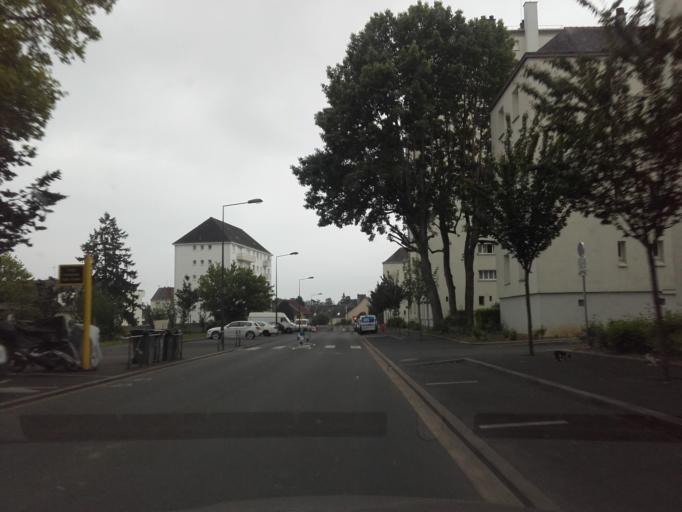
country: FR
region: Centre
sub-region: Departement d'Indre-et-Loire
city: Saint-Cyr-sur-Loire
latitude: 47.4130
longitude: 0.6875
